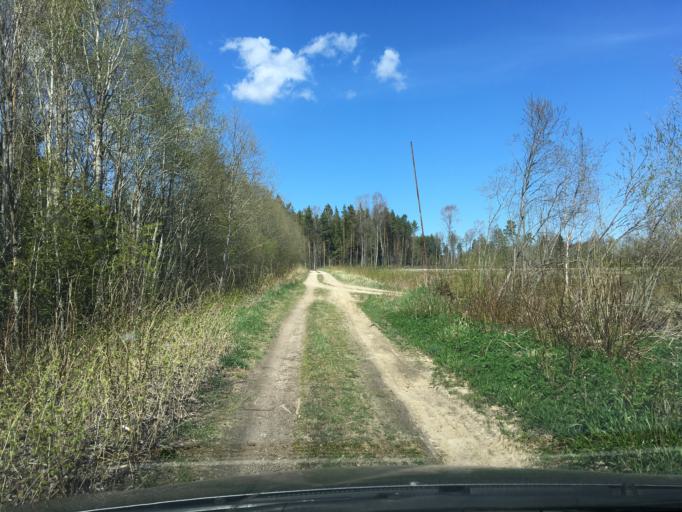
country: EE
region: Harju
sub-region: Raasiku vald
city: Arukula
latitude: 59.2083
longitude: 25.1191
